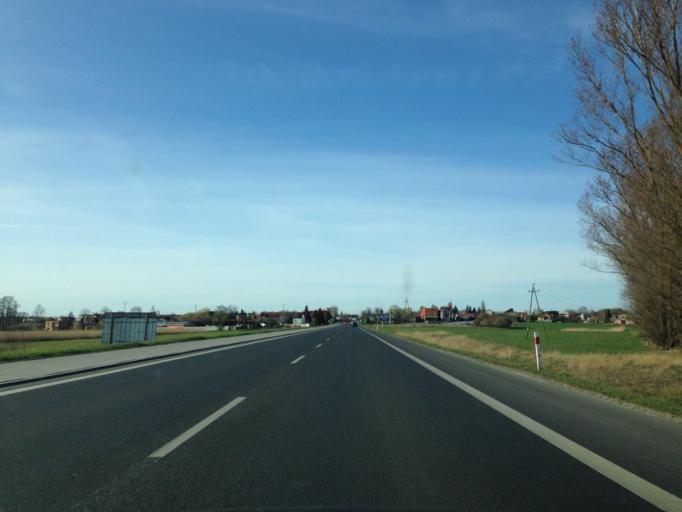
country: PL
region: Lodz Voivodeship
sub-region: Powiat leczycki
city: Leczyca
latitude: 52.0726
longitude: 19.1939
